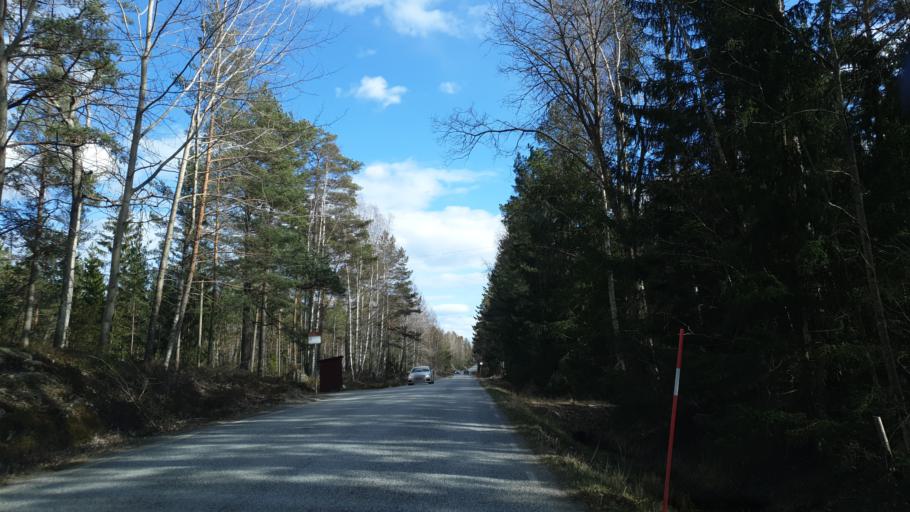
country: SE
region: Stockholm
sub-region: Varmdo Kommun
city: Mortnas
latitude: 59.2466
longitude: 18.4621
